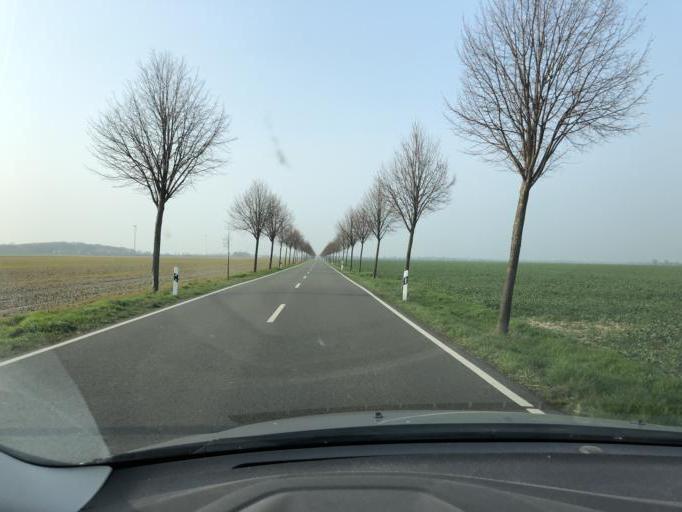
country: DE
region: Saxony-Anhalt
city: Brehna
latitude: 51.5713
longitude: 12.2019
